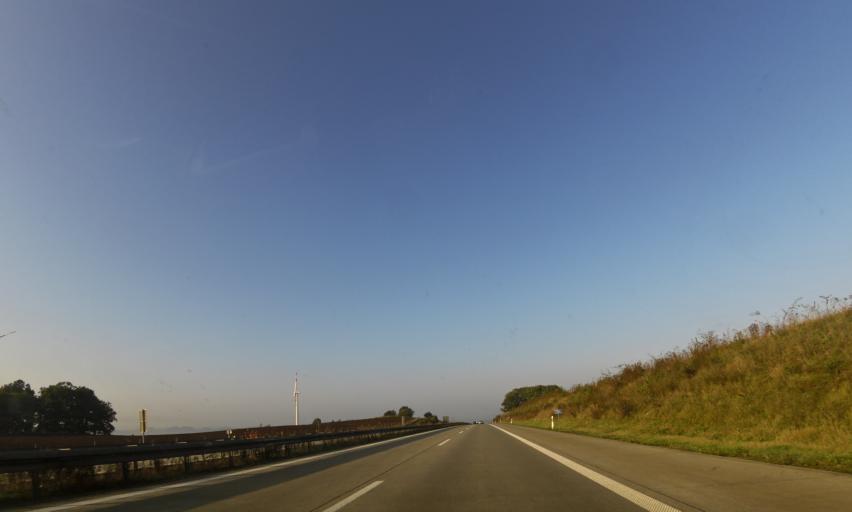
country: DE
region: Saxony
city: Reinsdorf
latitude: 50.6793
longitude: 12.5768
